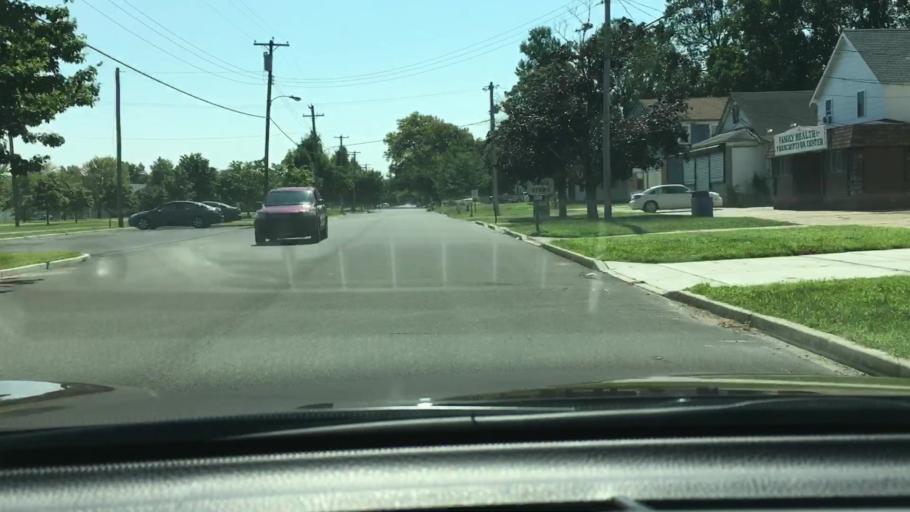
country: US
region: New Jersey
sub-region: Cape May County
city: Woodbine
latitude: 39.2407
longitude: -74.8144
